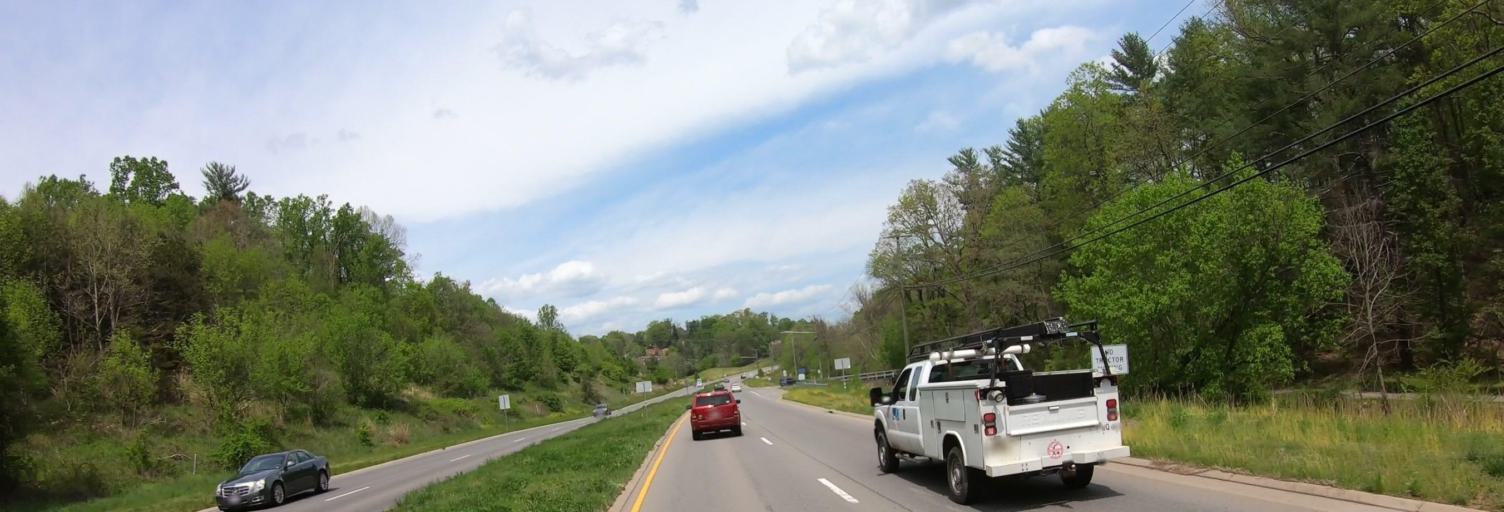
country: US
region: Virginia
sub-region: Roanoke County
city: Cave Spring
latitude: 37.2067
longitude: -80.0249
